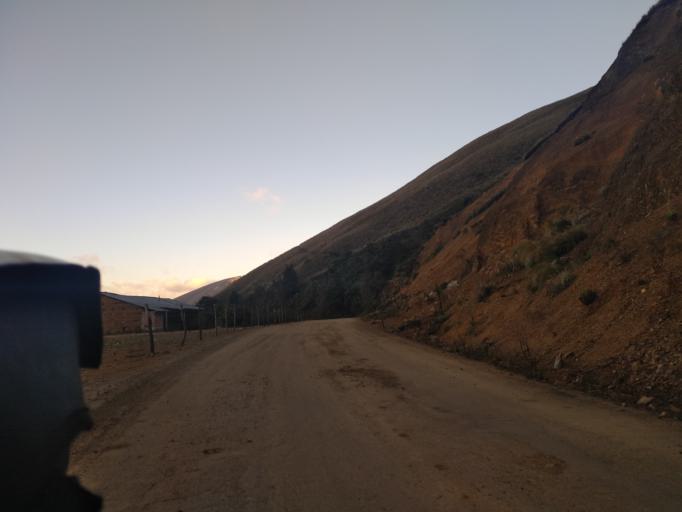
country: PE
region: Amazonas
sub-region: Provincia de Chachapoyas
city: Montevideo
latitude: -6.7224
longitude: -77.8772
